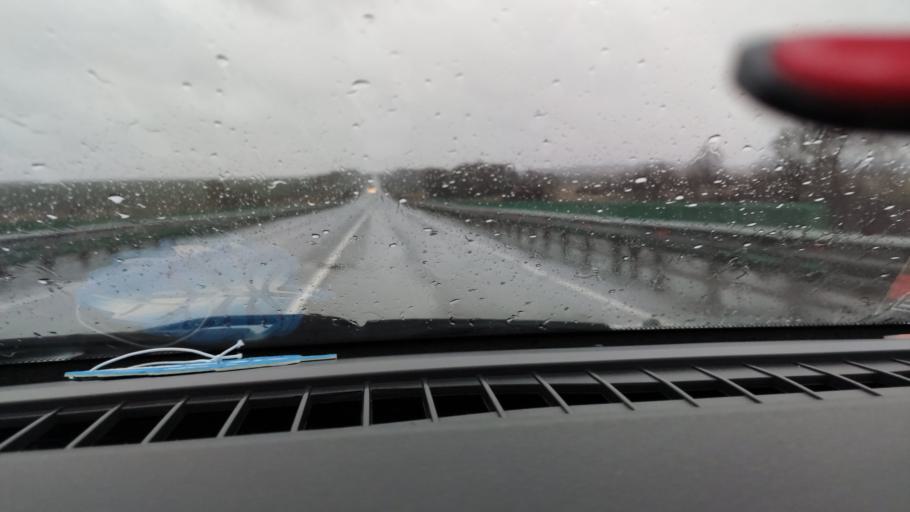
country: RU
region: Tatarstan
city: Mendeleyevsk
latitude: 55.9375
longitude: 52.2880
